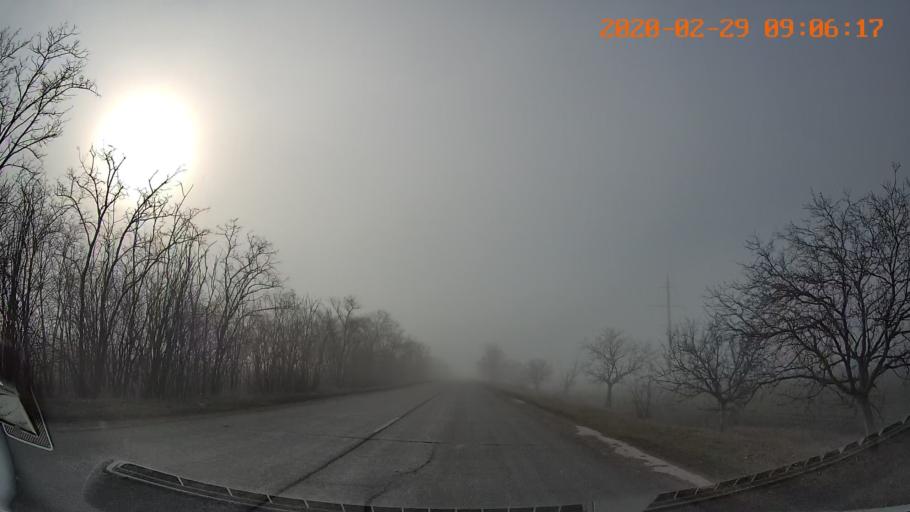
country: MD
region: Telenesti
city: Tiraspolul Nou
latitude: 46.8778
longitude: 29.7439
